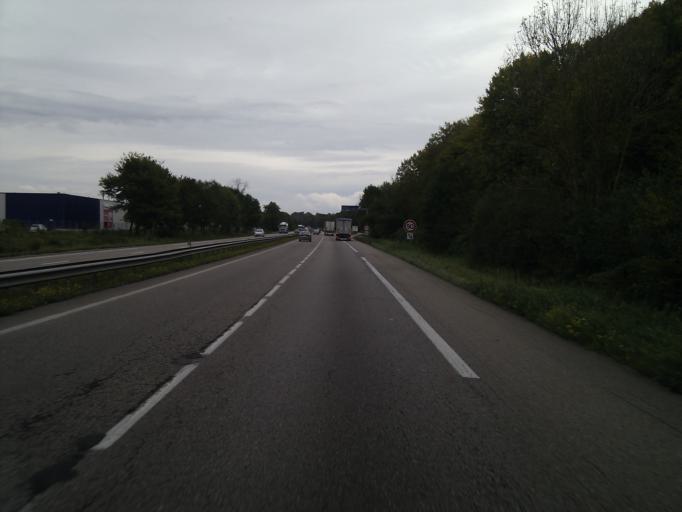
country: FR
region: Lorraine
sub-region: Departement de Meurthe-et-Moselle
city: Velaine-en-Haye
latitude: 48.6882
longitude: 6.0065
